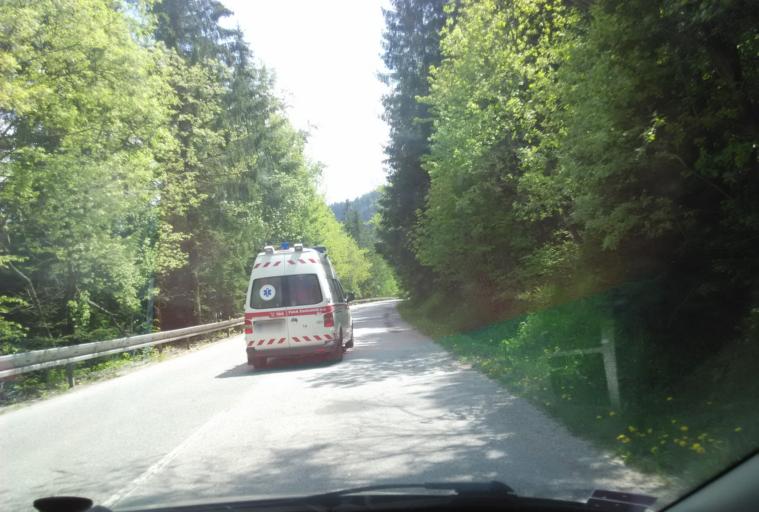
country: SK
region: Kosicky
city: Dobsina
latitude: 48.8564
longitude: 20.3806
